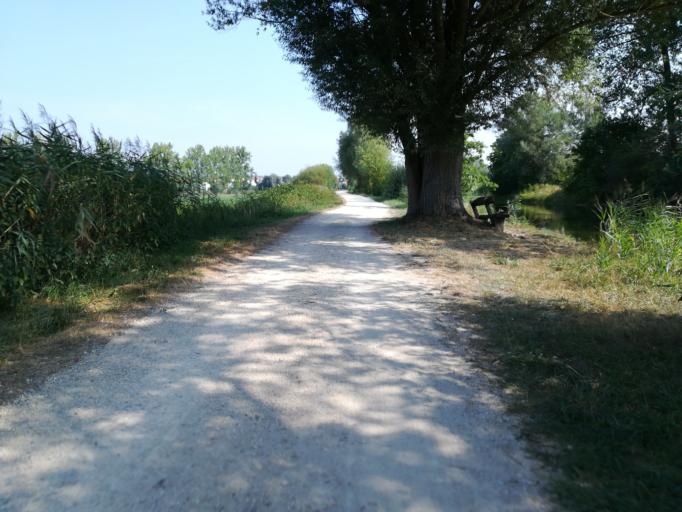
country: DE
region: Baden-Wuerttemberg
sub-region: Freiburg Region
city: Singen
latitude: 47.7852
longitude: 8.8362
